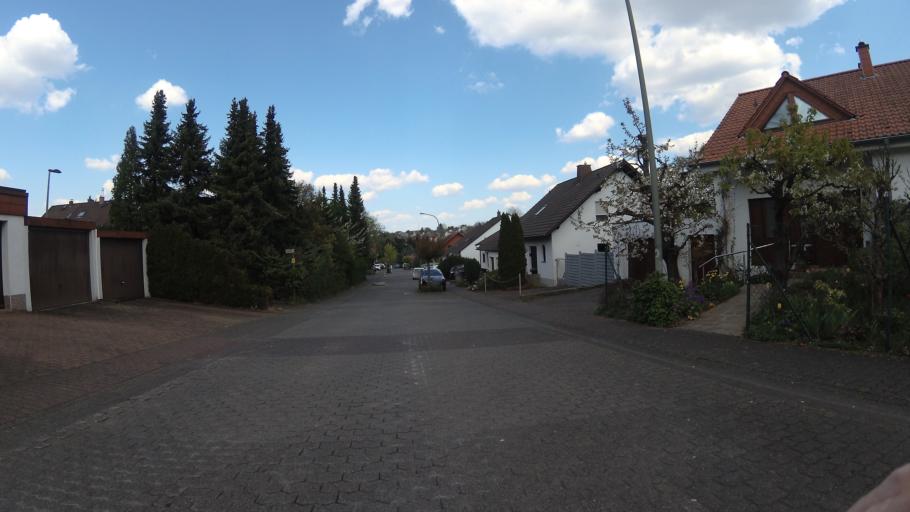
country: DE
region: Saarland
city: Riegelsberg
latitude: 49.3090
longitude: 6.9343
